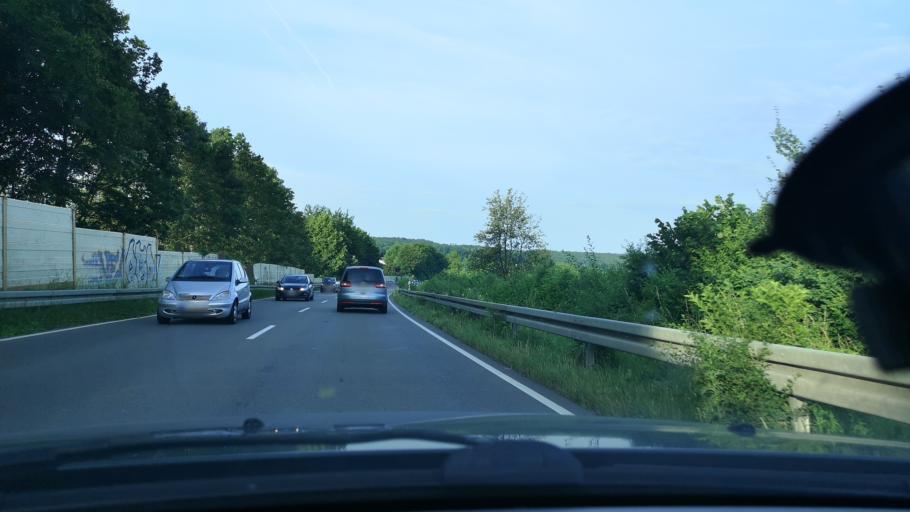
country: DE
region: Baden-Wuerttemberg
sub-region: Regierungsbezirk Stuttgart
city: Schlierbach
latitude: 48.6743
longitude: 9.5126
